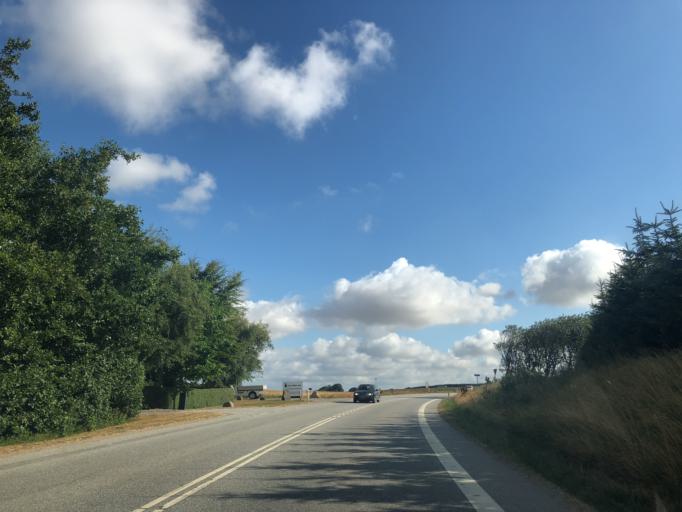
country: DK
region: Central Jutland
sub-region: Skive Kommune
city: Skive
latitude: 56.6249
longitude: 8.8832
